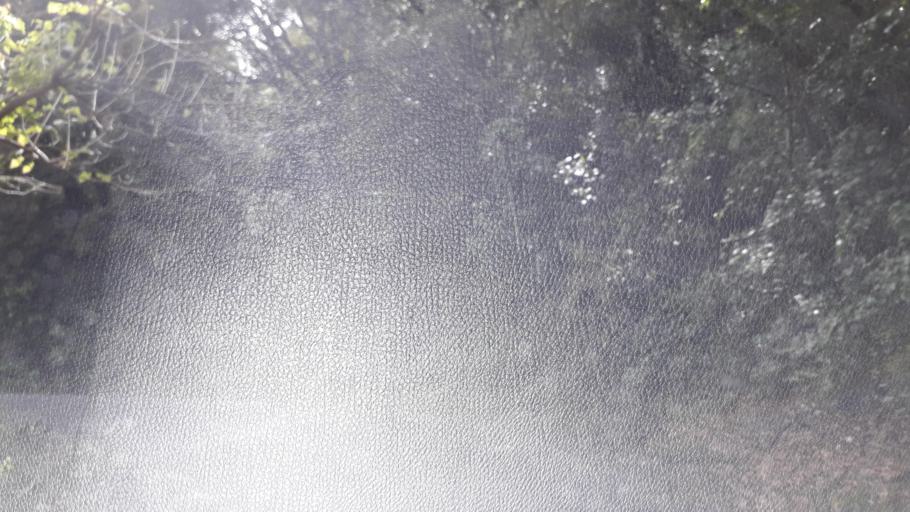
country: NZ
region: Northland
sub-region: Far North District
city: Taipa
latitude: -35.0995
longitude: 173.5494
